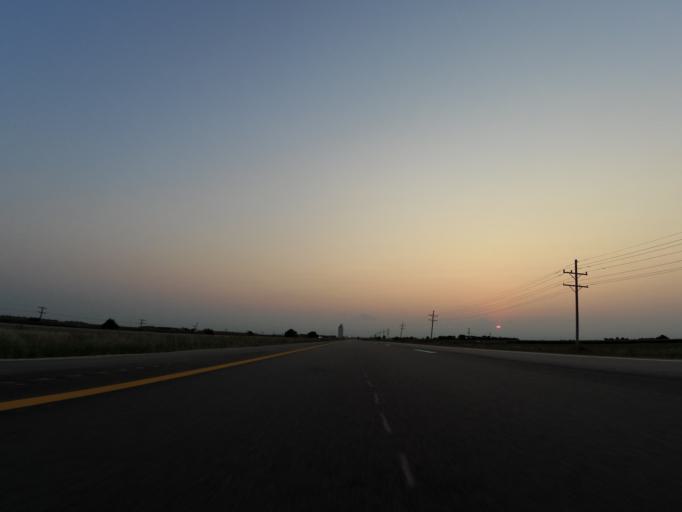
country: US
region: Kansas
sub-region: Reno County
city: South Hutchinson
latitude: 38.0006
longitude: -98.0258
